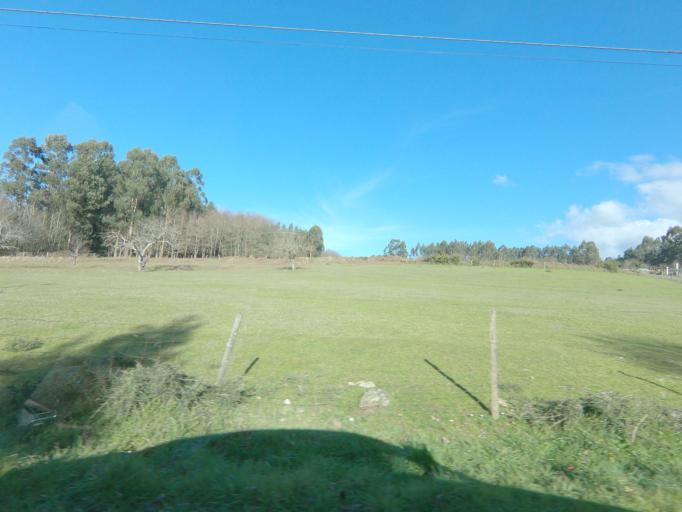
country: ES
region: Galicia
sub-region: Provincia da Coruna
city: Ribeira
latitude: 42.7076
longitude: -8.4303
